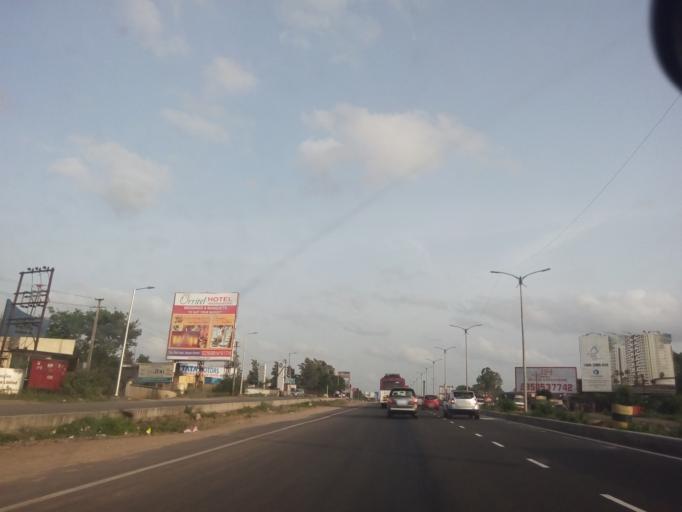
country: IN
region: Maharashtra
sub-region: Pune Division
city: Pimpri
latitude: 18.6259
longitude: 73.7443
